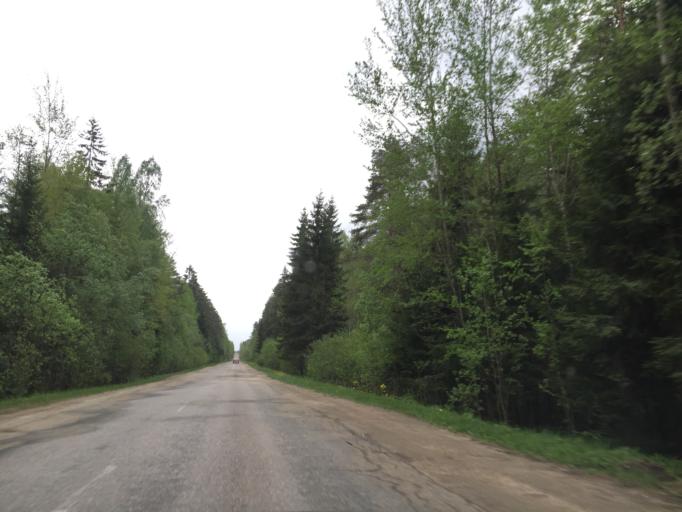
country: LV
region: Ogre
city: Ogre
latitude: 56.8541
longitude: 24.5675
